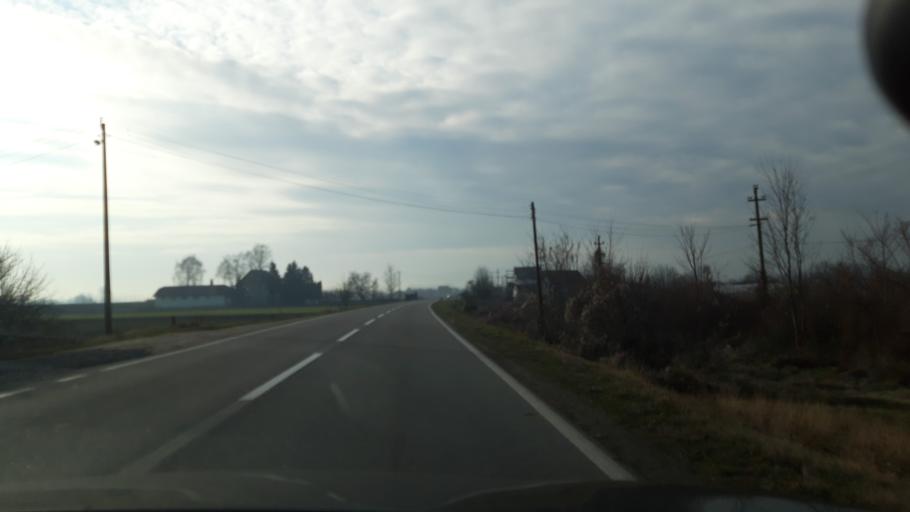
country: RS
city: Lesnica
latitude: 44.6301
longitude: 19.2729
